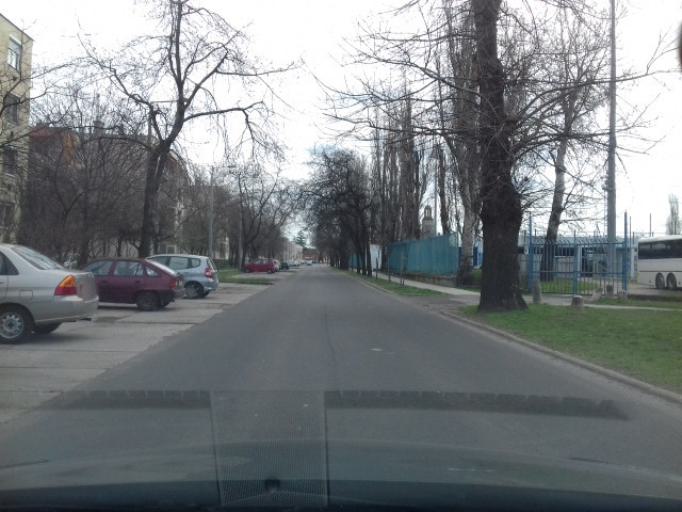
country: HU
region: Budapest
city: Budapest XV. keruelet
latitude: 47.5633
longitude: 19.1209
